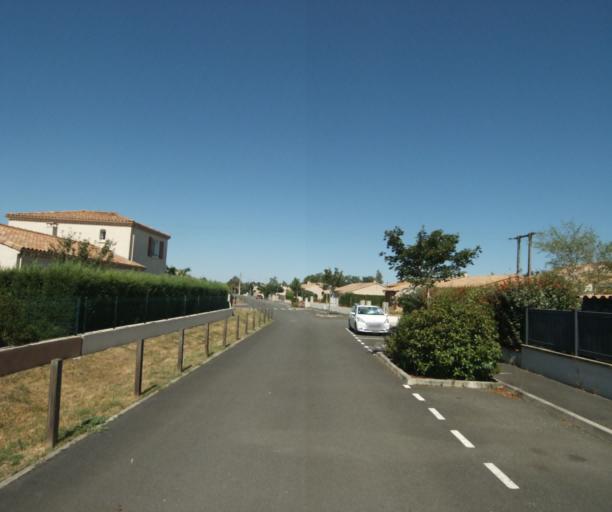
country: FR
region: Midi-Pyrenees
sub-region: Departement de la Haute-Garonne
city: Revel
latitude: 43.4631
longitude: 1.9894
